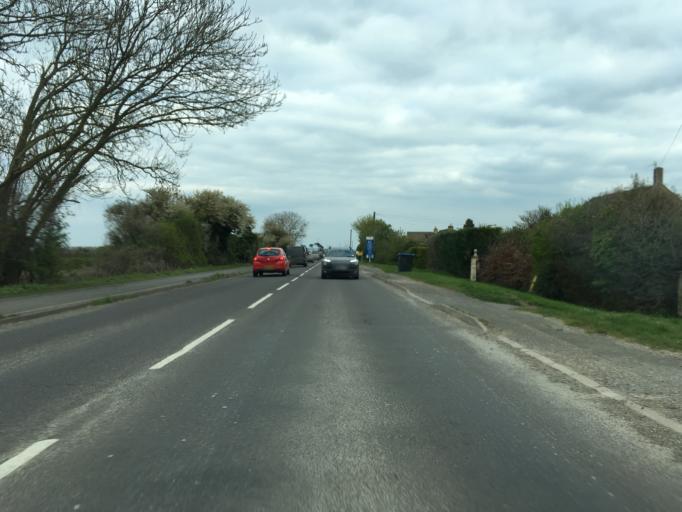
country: GB
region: England
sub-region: Oxfordshire
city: Witney
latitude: 51.7943
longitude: -1.5270
